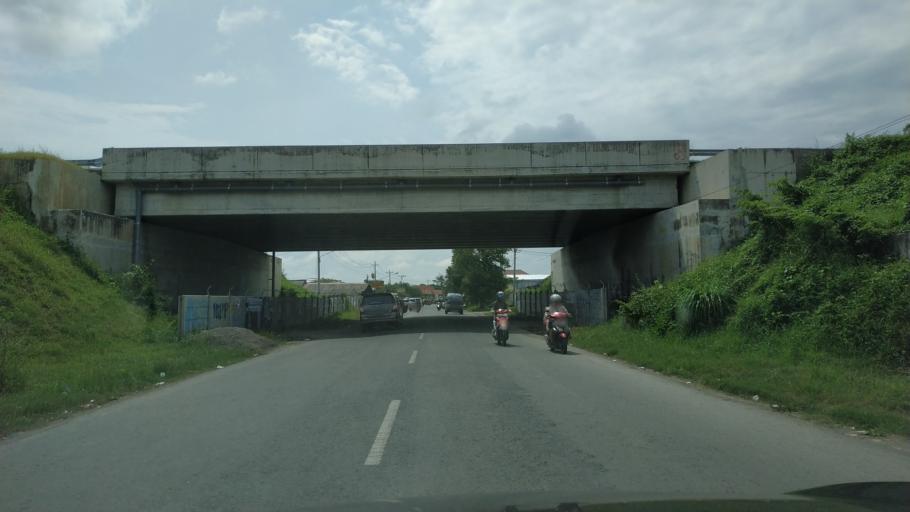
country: ID
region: Central Java
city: Adiwerna
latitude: -6.9355
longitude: 109.1251
